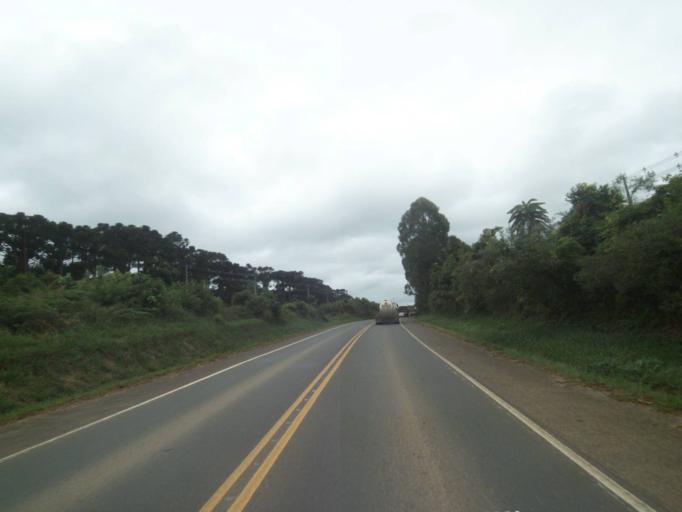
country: BR
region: Parana
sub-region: Telemaco Borba
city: Telemaco Borba
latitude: -24.3657
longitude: -50.6586
